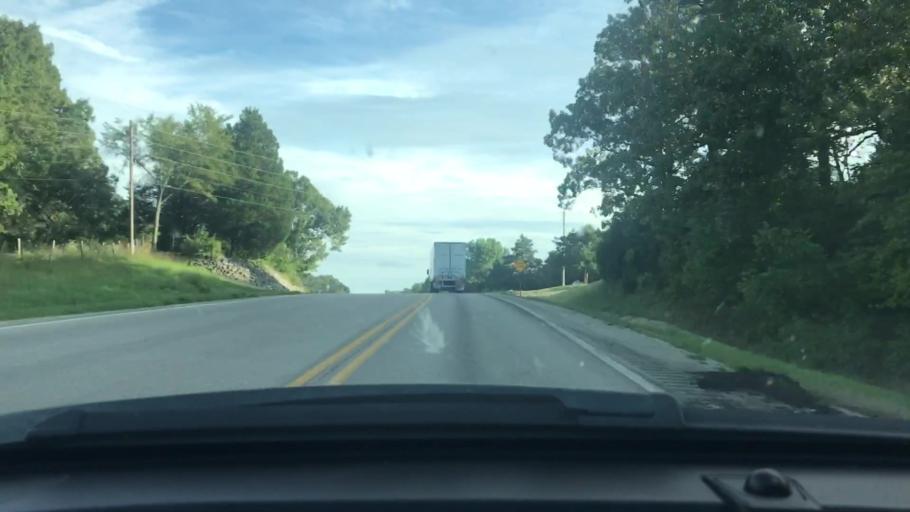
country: US
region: Arkansas
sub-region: Lawrence County
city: Hoxie
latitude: 36.1561
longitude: -91.1617
